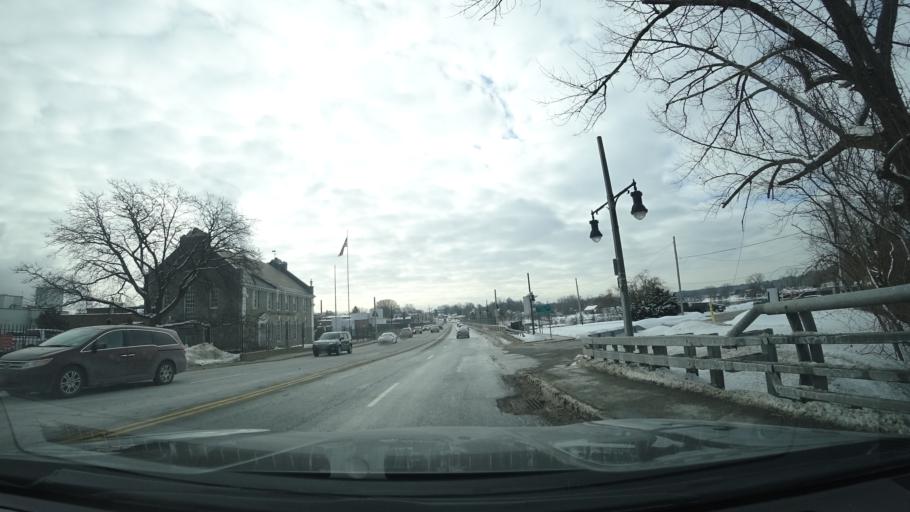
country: US
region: New York
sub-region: Warren County
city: Glens Falls
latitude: 43.3072
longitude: -73.6421
